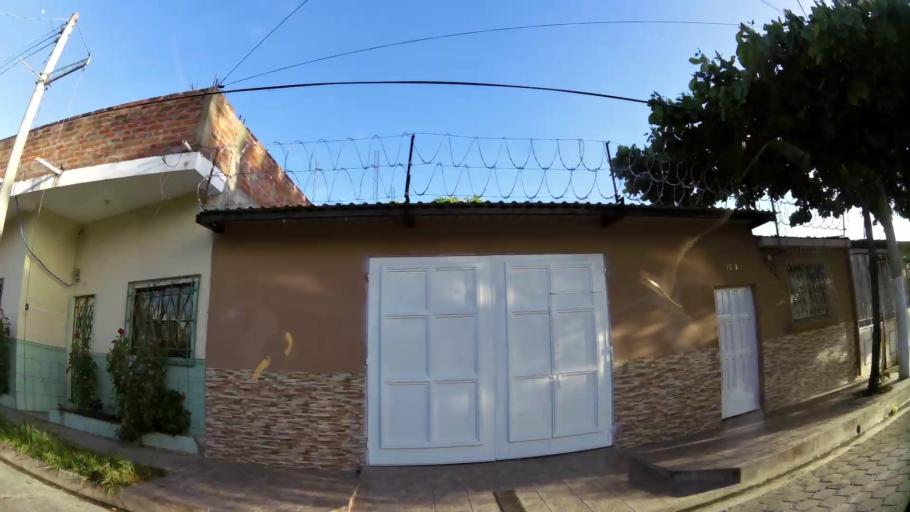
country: SV
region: Santa Ana
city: Metapan
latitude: 14.3323
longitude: -89.4524
